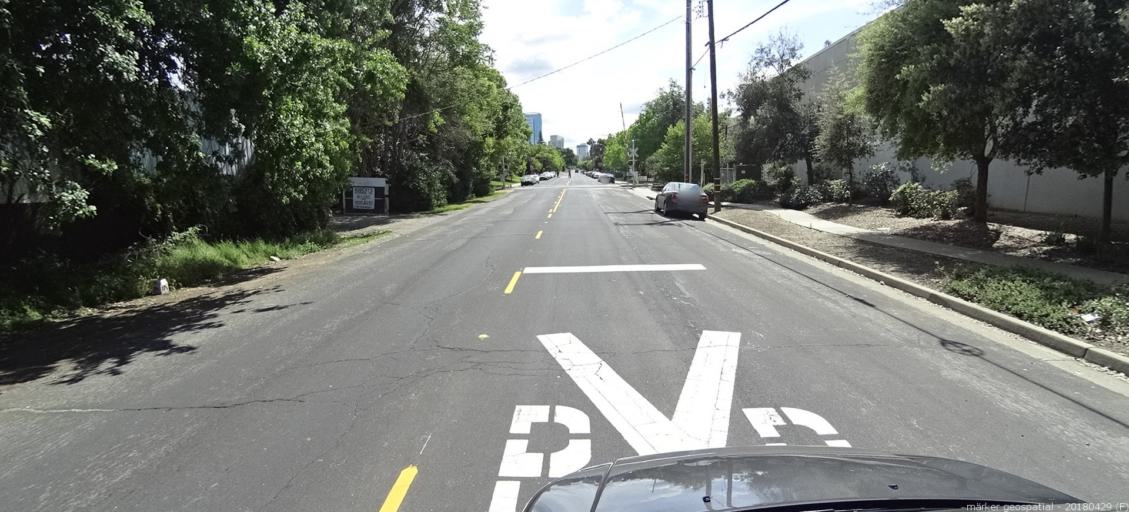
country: US
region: California
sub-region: Yolo County
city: West Sacramento
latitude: 38.5855
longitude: -121.5189
